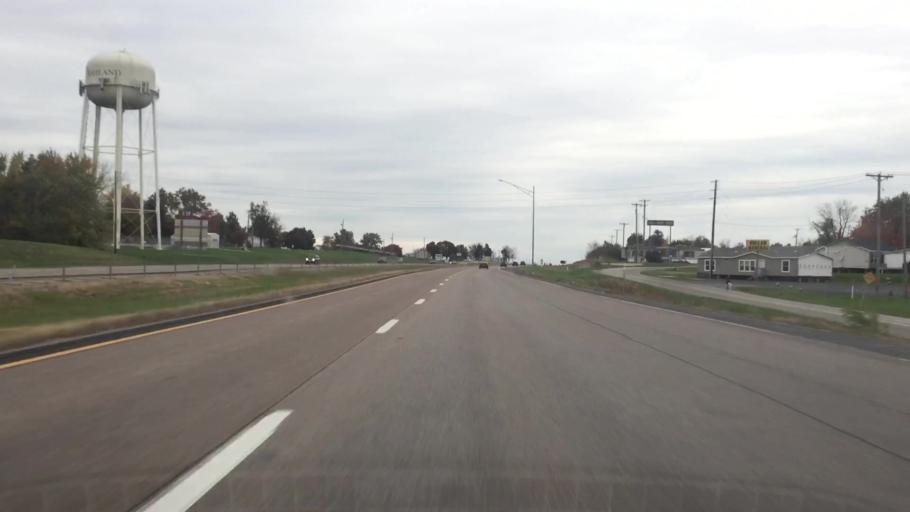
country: US
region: Missouri
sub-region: Boone County
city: Ashland
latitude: 38.7773
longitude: -92.2522
